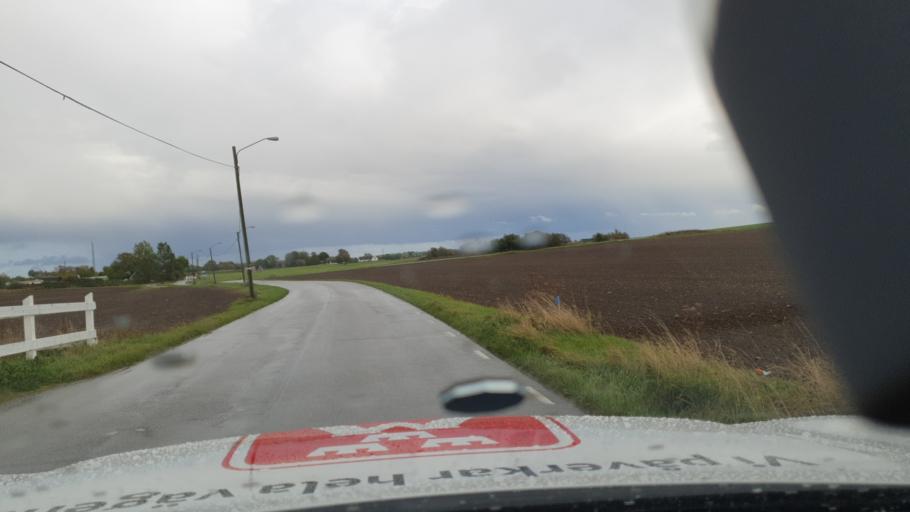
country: SE
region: Skane
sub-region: Malmo
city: Oxie
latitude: 55.5233
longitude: 13.0541
